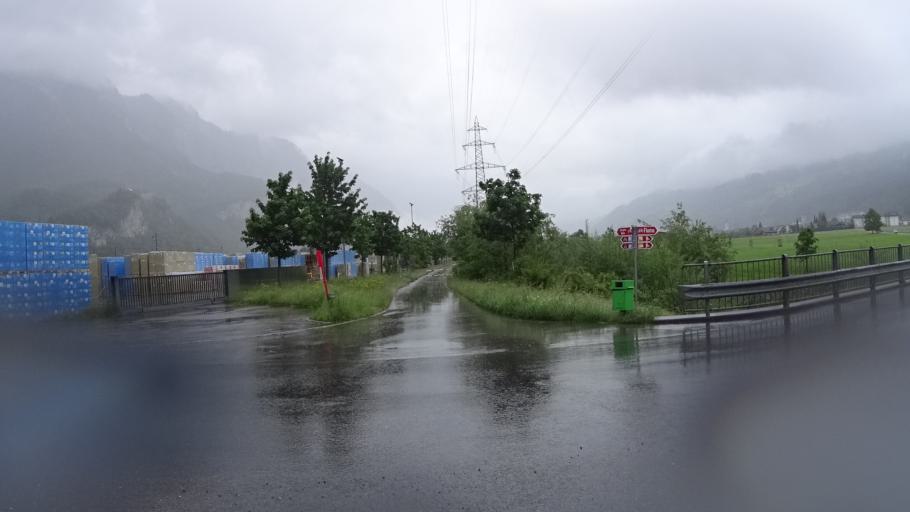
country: CH
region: Saint Gallen
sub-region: Wahlkreis Sarganserland
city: Flums
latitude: 47.1027
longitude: 9.3382
